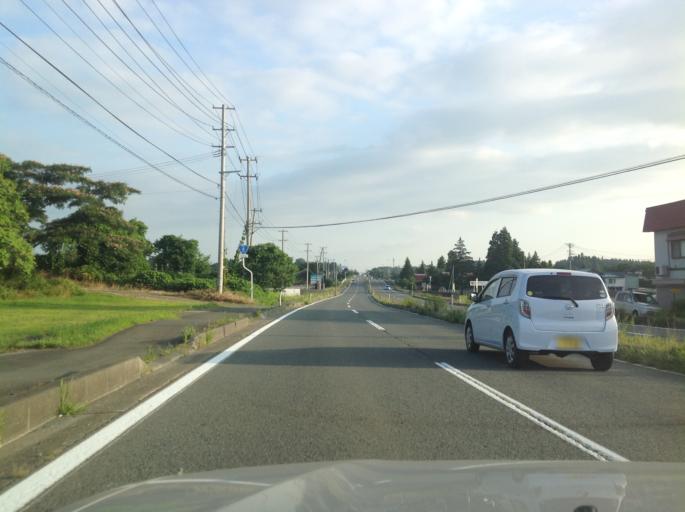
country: JP
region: Iwate
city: Hanamaki
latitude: 39.5240
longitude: 141.1622
